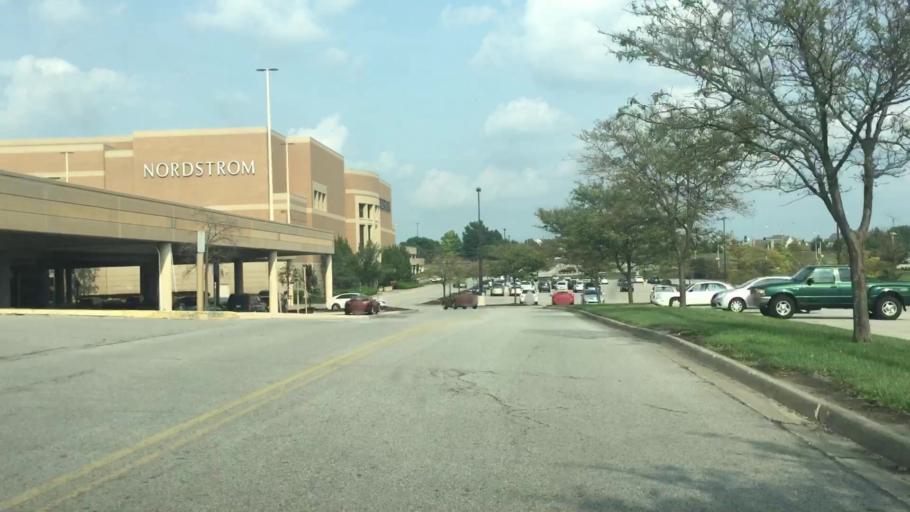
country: US
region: Kansas
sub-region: Johnson County
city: Lenexa
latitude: 38.9518
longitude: -94.7202
